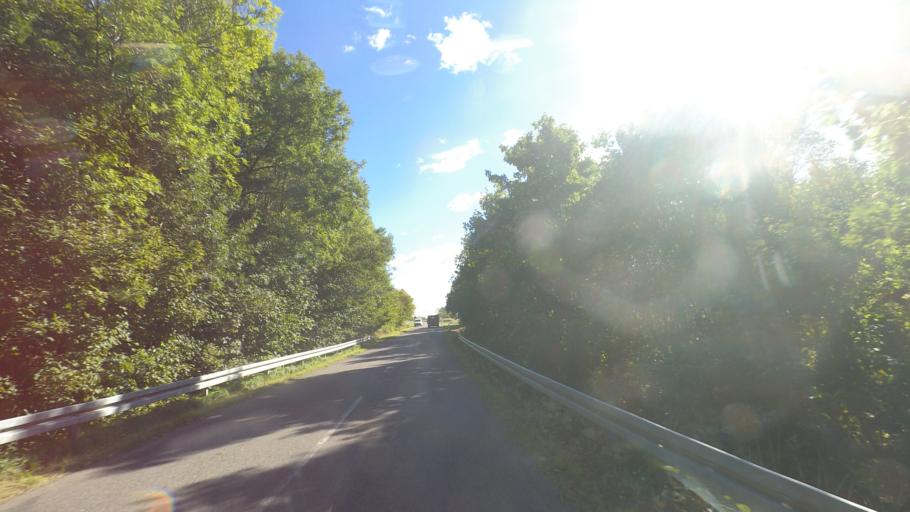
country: DK
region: Capital Region
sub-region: Bornholm Kommune
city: Akirkeby
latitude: 55.1324
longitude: 15.0223
